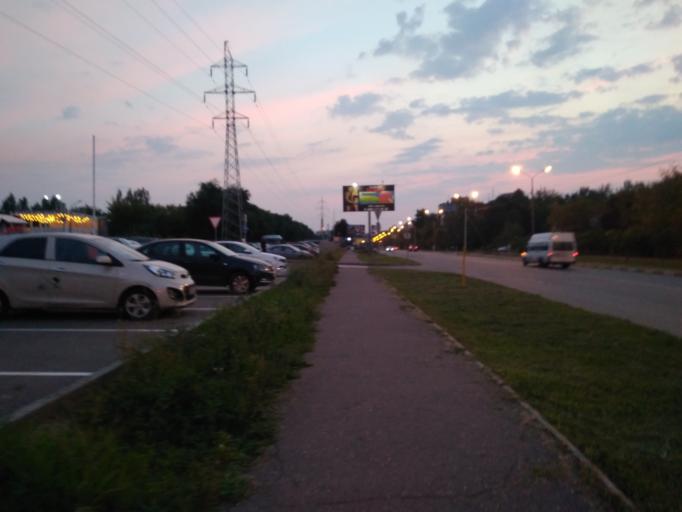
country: RU
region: Moskovskaya
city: Zhukovskiy
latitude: 55.6017
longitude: 38.1074
